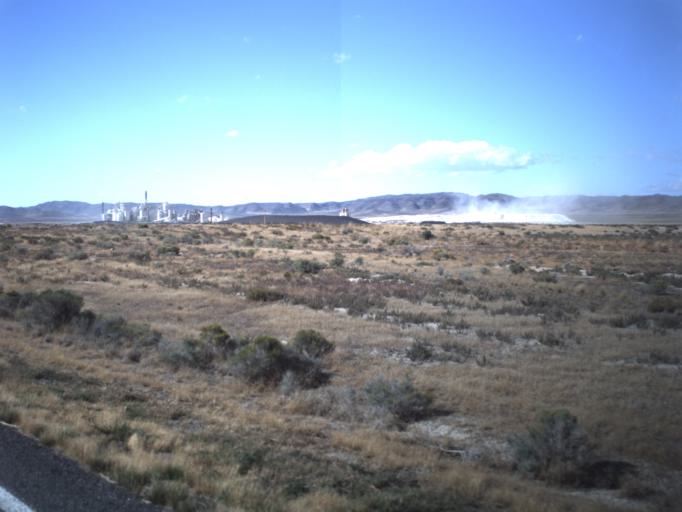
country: US
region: Utah
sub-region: Millard County
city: Delta
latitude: 38.9510
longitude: -112.8060
